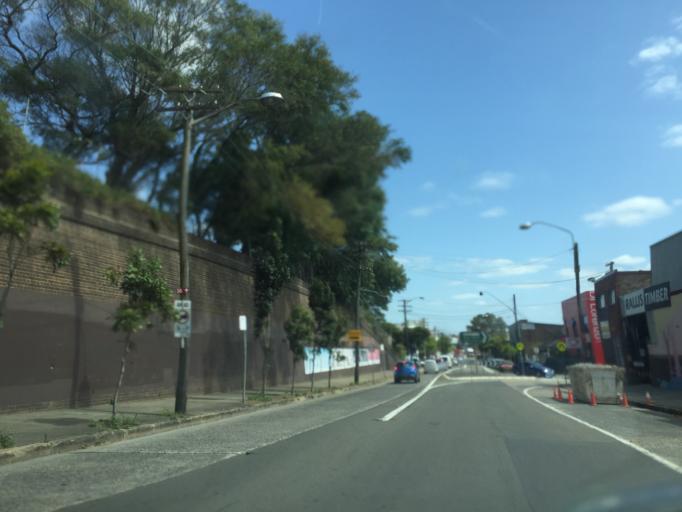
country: AU
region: New South Wales
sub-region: Marrickville
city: Marrickville
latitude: -33.9150
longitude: 151.1643
